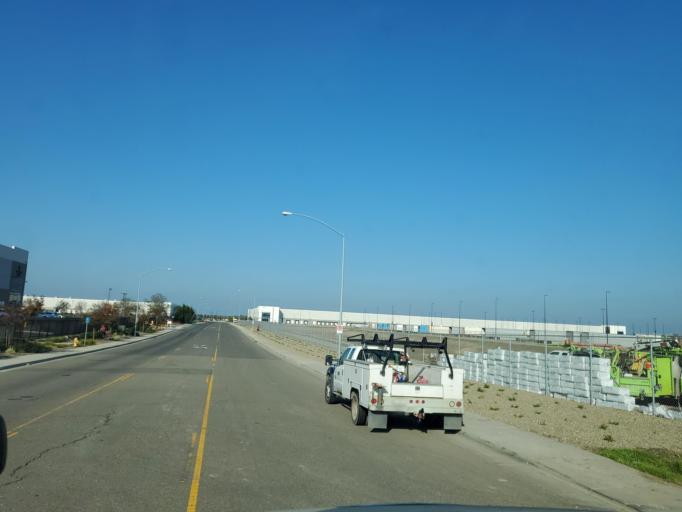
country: US
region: California
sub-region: San Joaquin County
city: Kennedy
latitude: 37.9090
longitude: -121.1932
